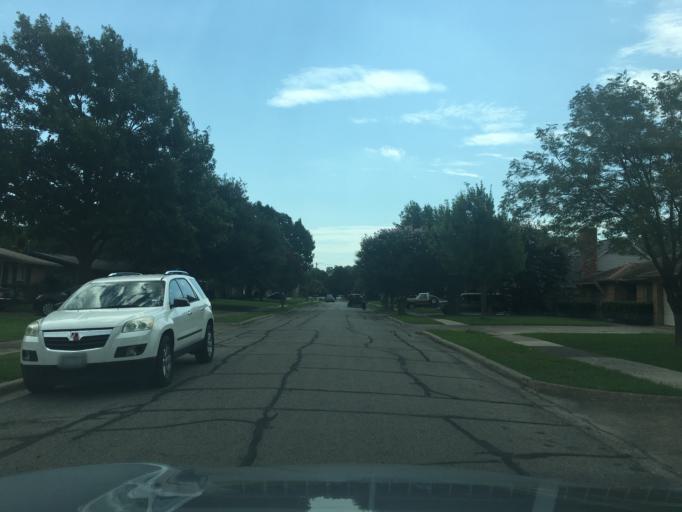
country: US
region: Texas
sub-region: Dallas County
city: Farmers Branch
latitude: 32.9283
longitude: -96.8673
